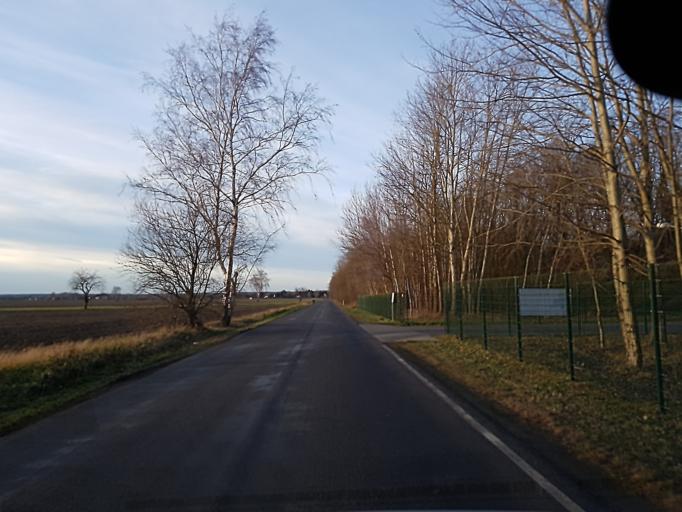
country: DE
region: Brandenburg
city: Finsterwalde
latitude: 51.6026
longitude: 13.7267
